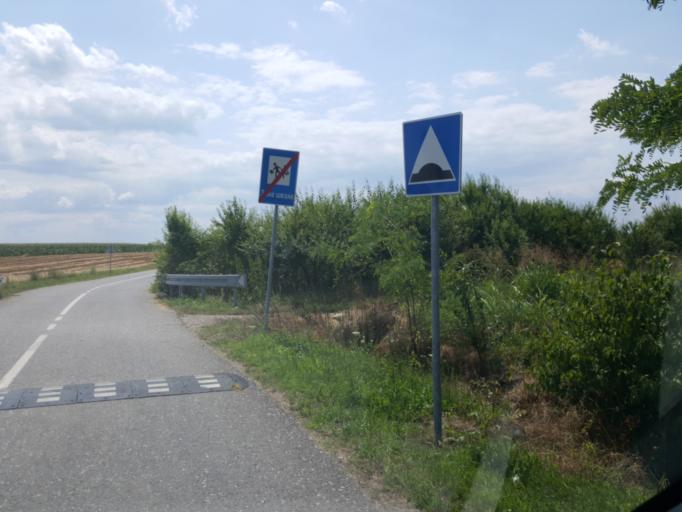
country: RS
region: Autonomna Pokrajina Vojvodina
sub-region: Sremski Okrug
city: Pecinci
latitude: 44.8437
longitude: 19.9571
